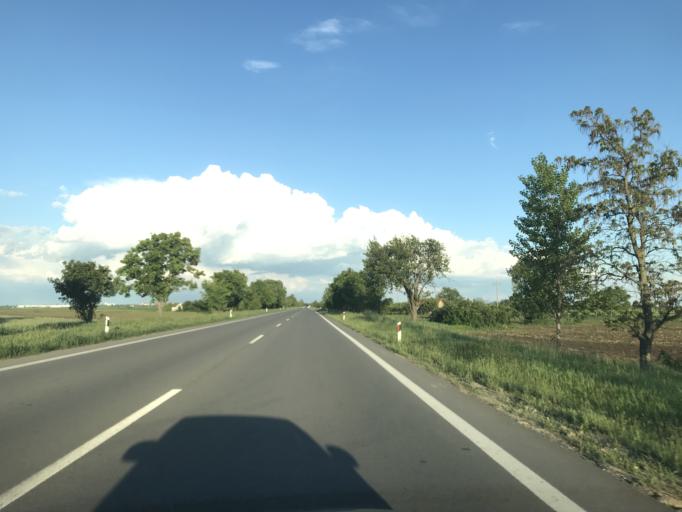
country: RS
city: Aradac
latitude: 45.3879
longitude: 20.3130
